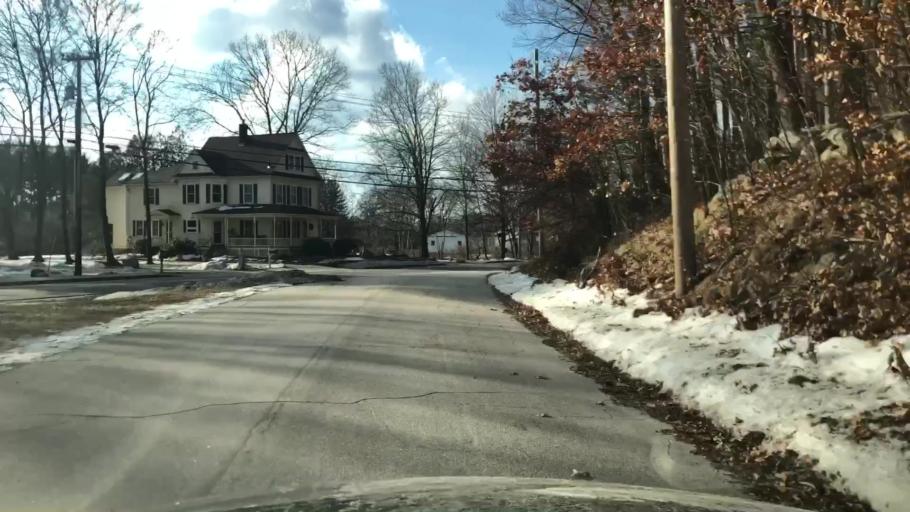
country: US
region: New Hampshire
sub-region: Hillsborough County
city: Milford
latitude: 42.8404
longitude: -71.6559
